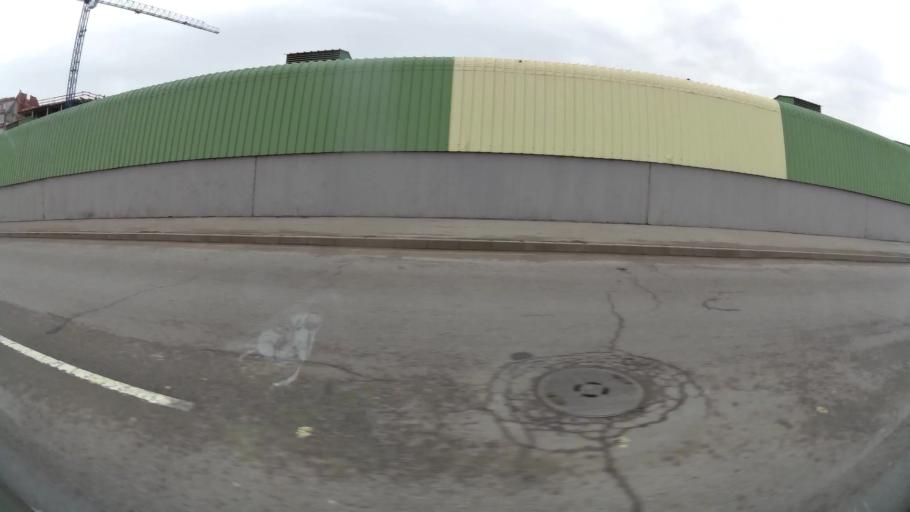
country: BG
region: Sofia-Capital
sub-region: Stolichna Obshtina
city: Sofia
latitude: 42.7399
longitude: 23.2754
